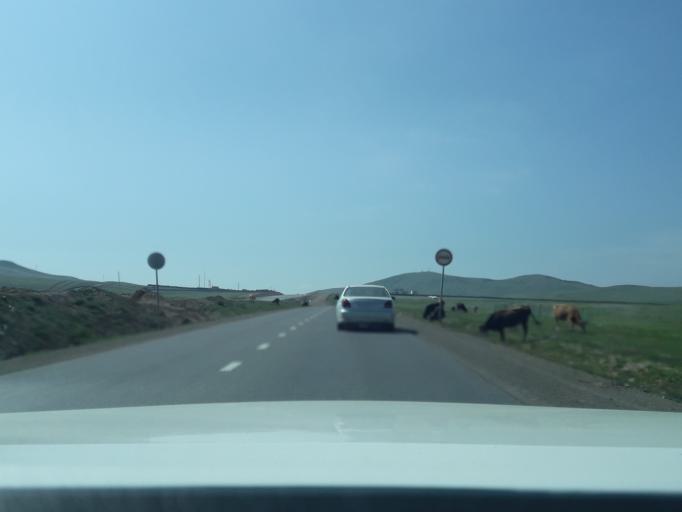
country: MN
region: Ulaanbaatar
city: Ulaanbaatar
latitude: 47.8116
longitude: 106.7531
